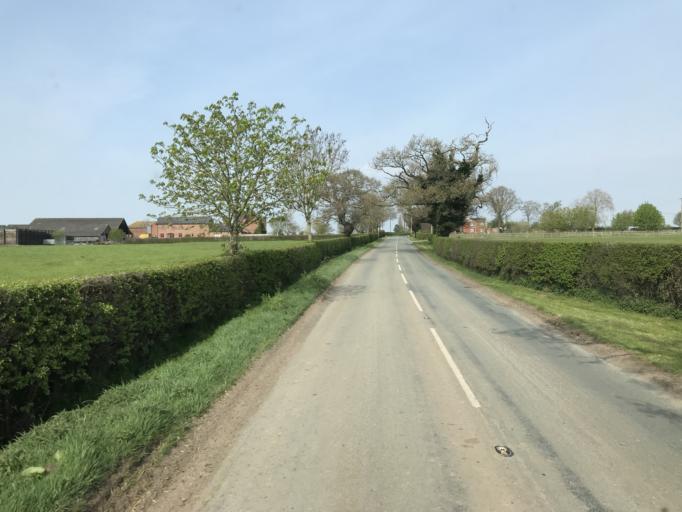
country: GB
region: England
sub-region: Cheshire West and Chester
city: Eccleston
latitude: 53.1572
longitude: -2.8618
